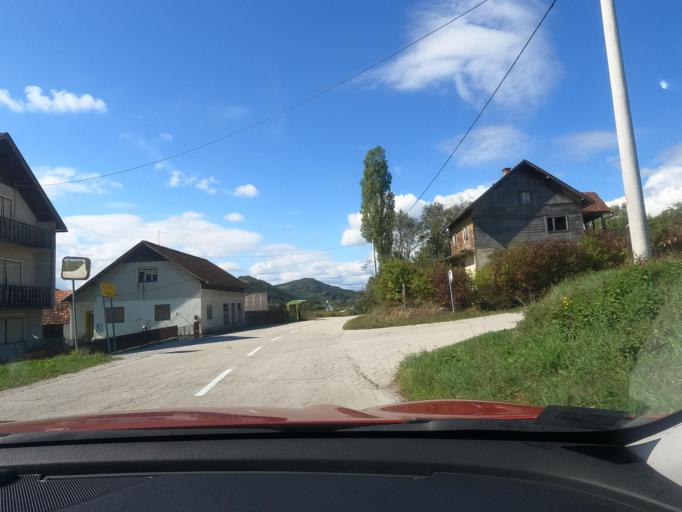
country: BA
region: Federation of Bosnia and Herzegovina
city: Podzvizd
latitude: 45.2237
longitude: 15.8803
